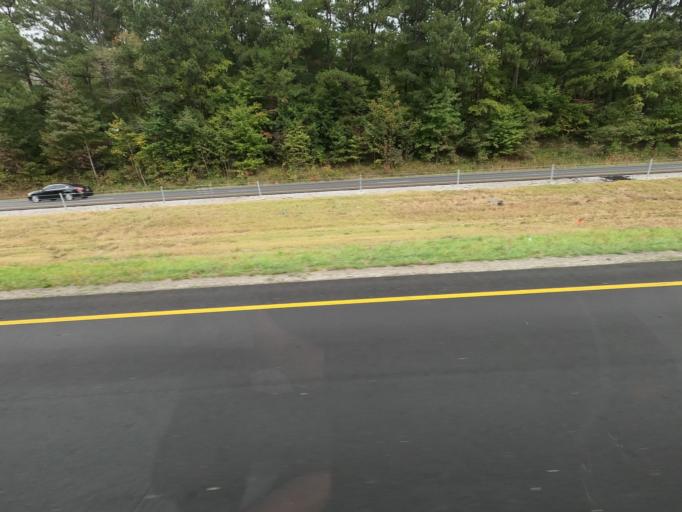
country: US
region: Tennessee
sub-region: Dickson County
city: Burns
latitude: 36.0188
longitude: -87.3429
